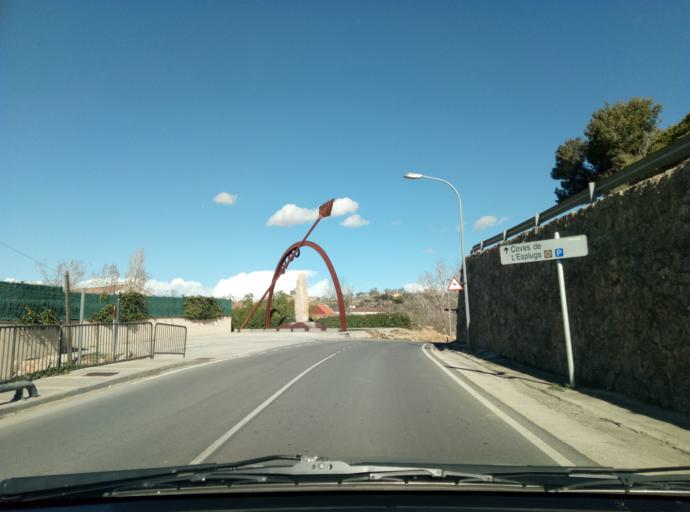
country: ES
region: Catalonia
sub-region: Provincia de Tarragona
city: Vimbodi
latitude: 41.3982
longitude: 1.1023
